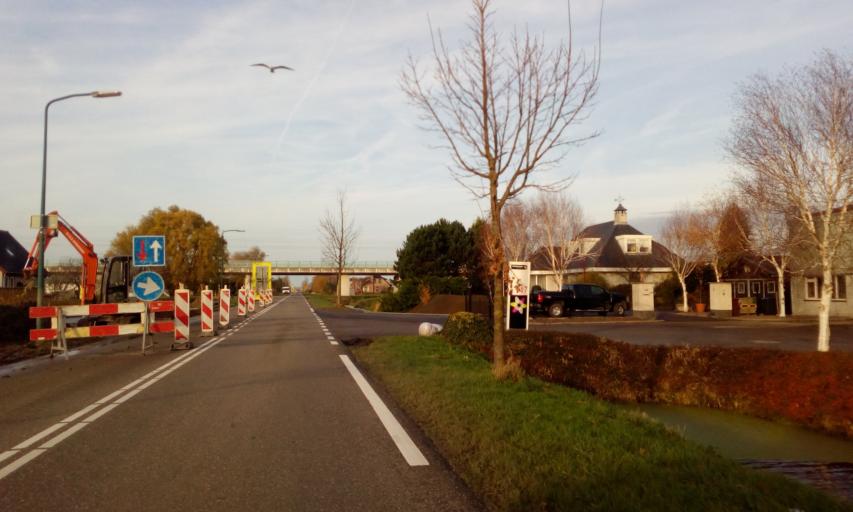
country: NL
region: South Holland
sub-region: Gemeente Lansingerland
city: Bleiswijk
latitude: 52.0227
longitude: 4.5186
